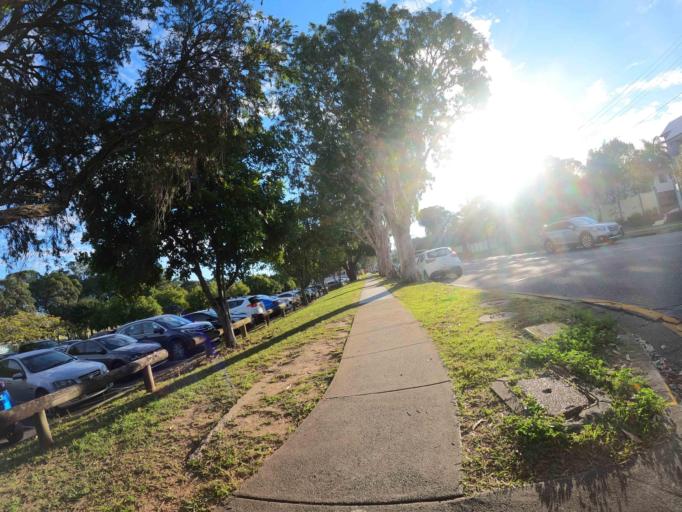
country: AU
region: Queensland
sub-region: Brisbane
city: Windsor
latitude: -27.4410
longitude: 153.0255
